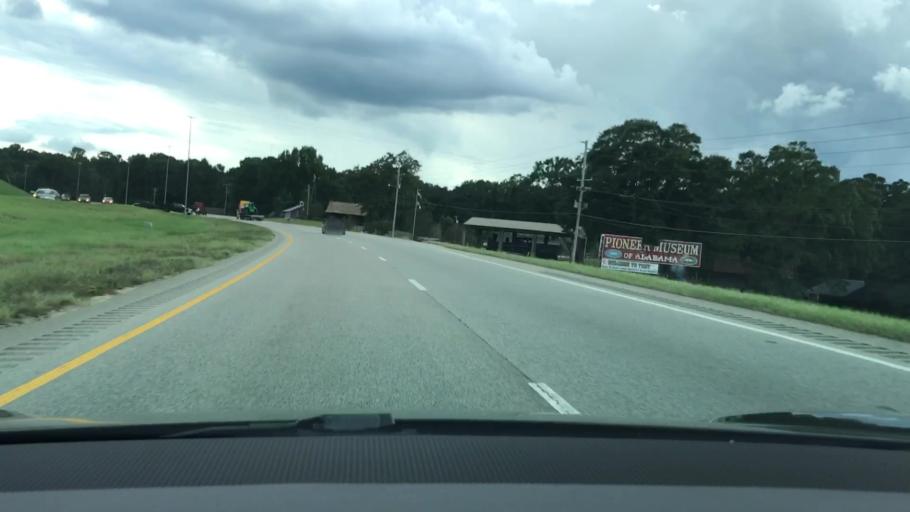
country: US
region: Alabama
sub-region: Pike County
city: Troy
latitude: 31.8265
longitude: -85.9946
